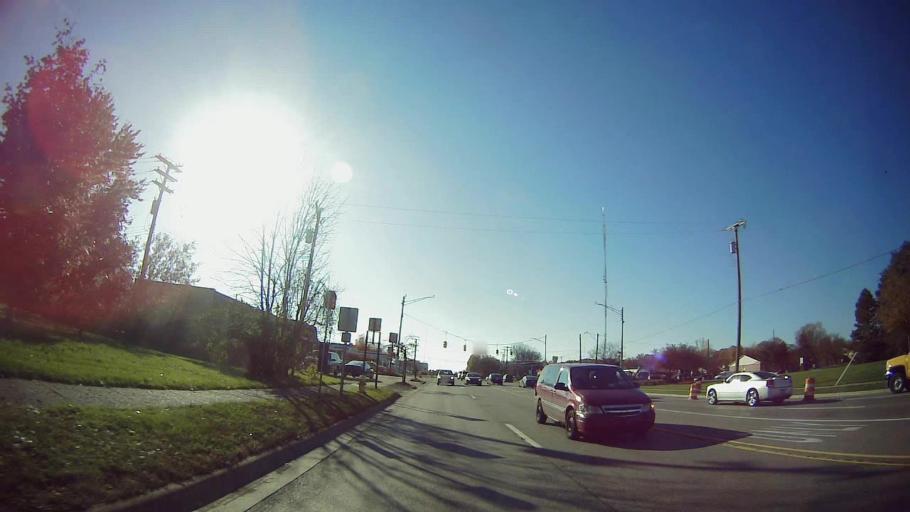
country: US
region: Michigan
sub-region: Oakland County
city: Lathrup Village
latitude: 42.4888
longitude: -83.2023
